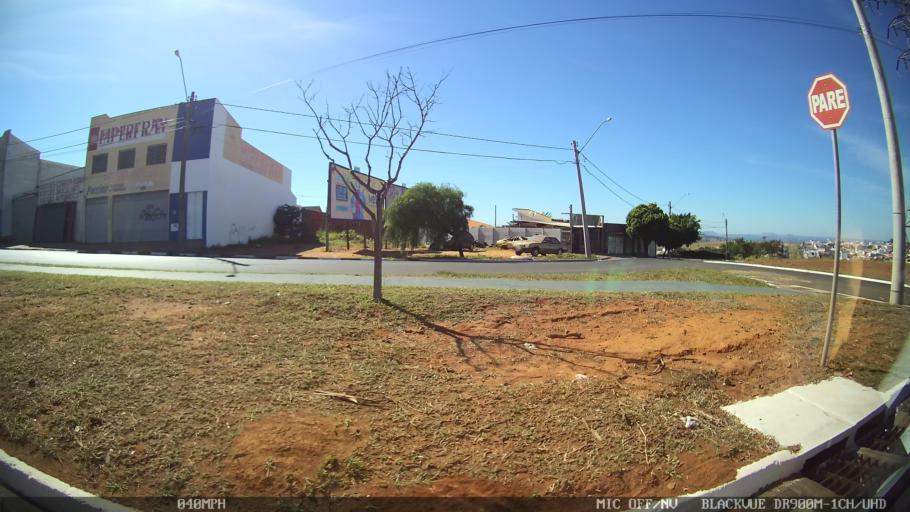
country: BR
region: Sao Paulo
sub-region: Franca
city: Franca
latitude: -20.5440
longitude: -47.3593
